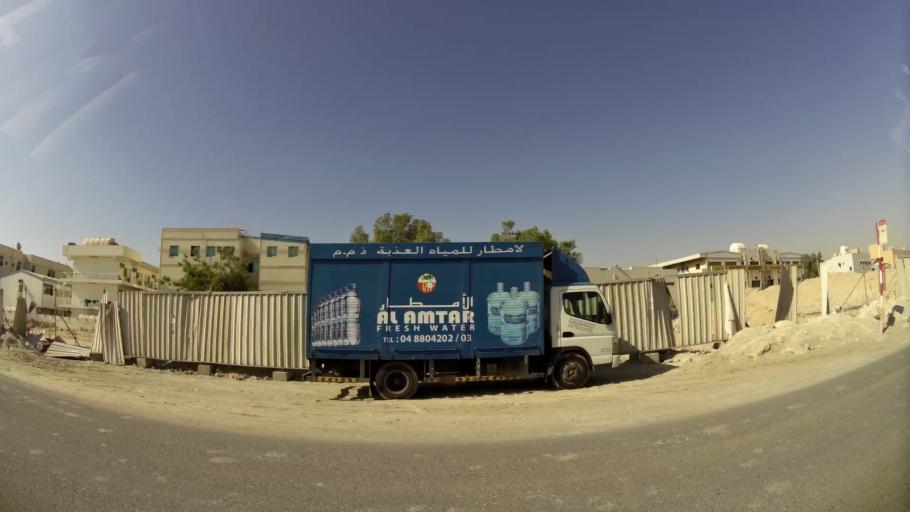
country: AE
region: Dubai
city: Dubai
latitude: 24.9996
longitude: 55.1062
